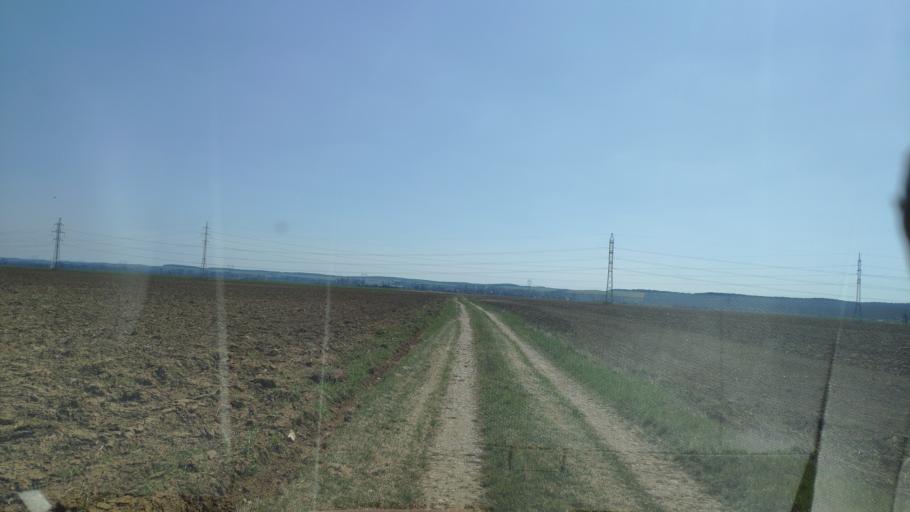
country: SK
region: Kosicky
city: Moldava nad Bodvou
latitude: 48.6010
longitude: 20.9447
